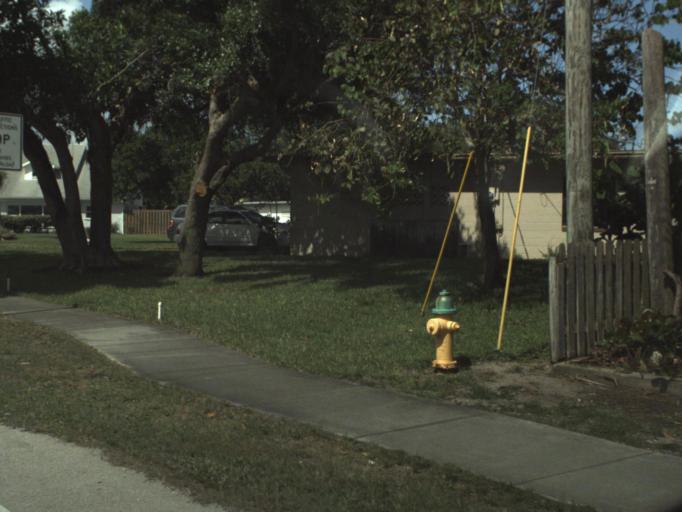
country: US
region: Florida
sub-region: Brevard County
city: Cocoa Beach
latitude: 28.3598
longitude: -80.6077
